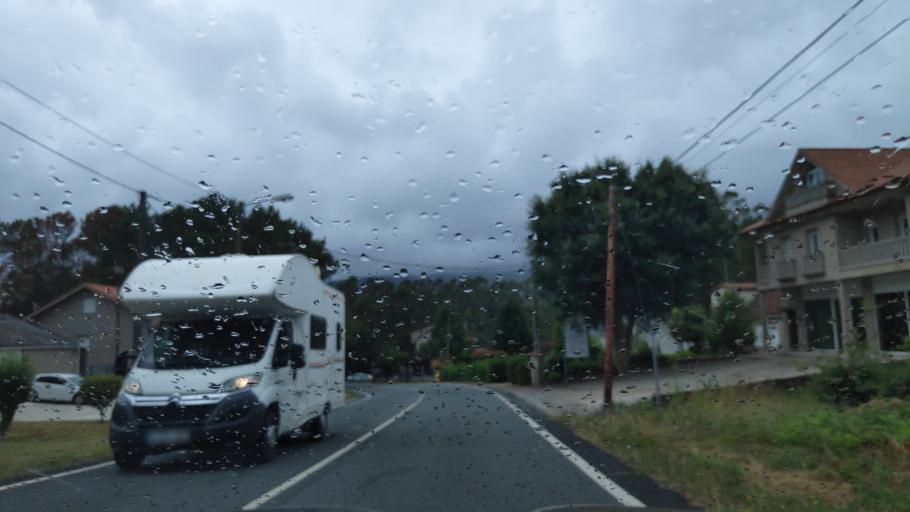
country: ES
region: Galicia
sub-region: Provincia de Pontevedra
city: Catoira
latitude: 42.6929
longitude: -8.7735
